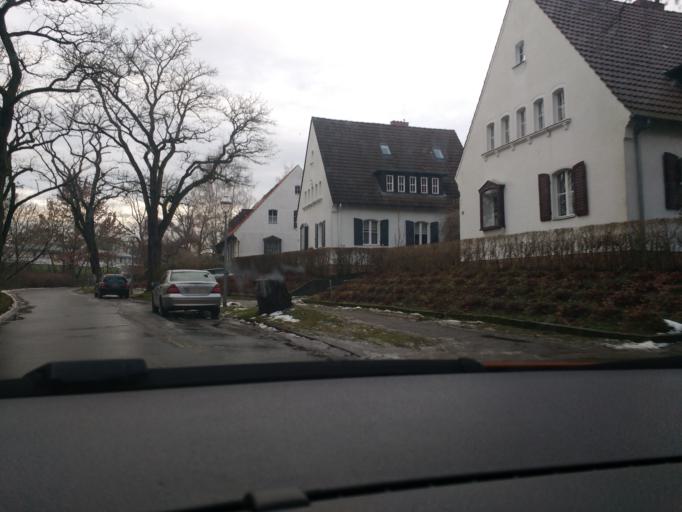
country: DE
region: Berlin
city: Zehlendorf Bezirk
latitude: 52.4345
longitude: 13.2398
